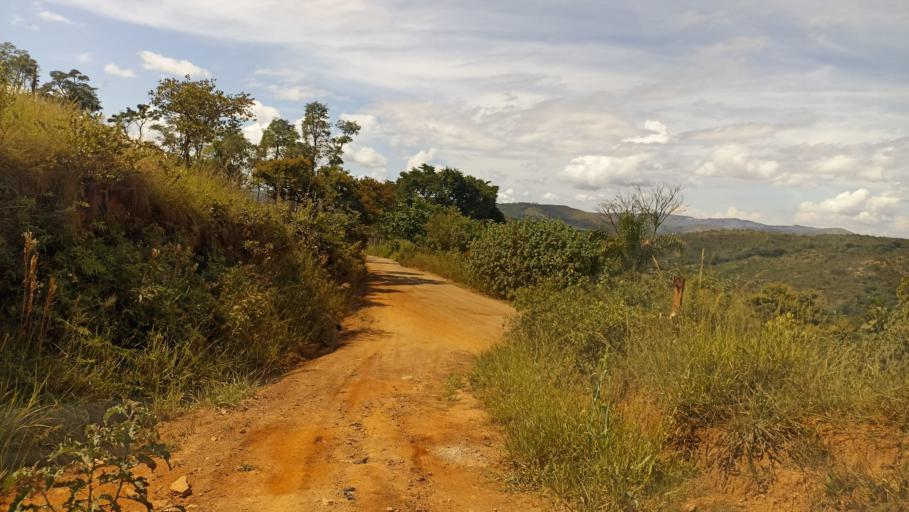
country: BR
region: Minas Gerais
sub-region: Itabirito
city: Itabirito
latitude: -20.3522
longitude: -43.7226
